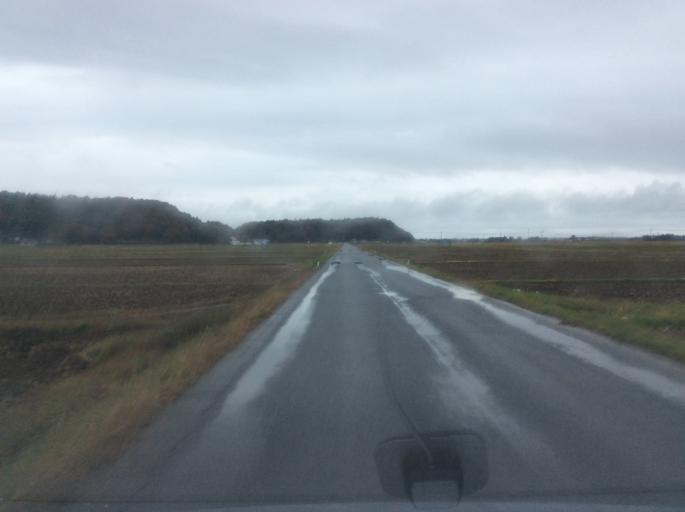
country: JP
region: Fukushima
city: Iwaki
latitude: 37.0906
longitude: 140.9427
